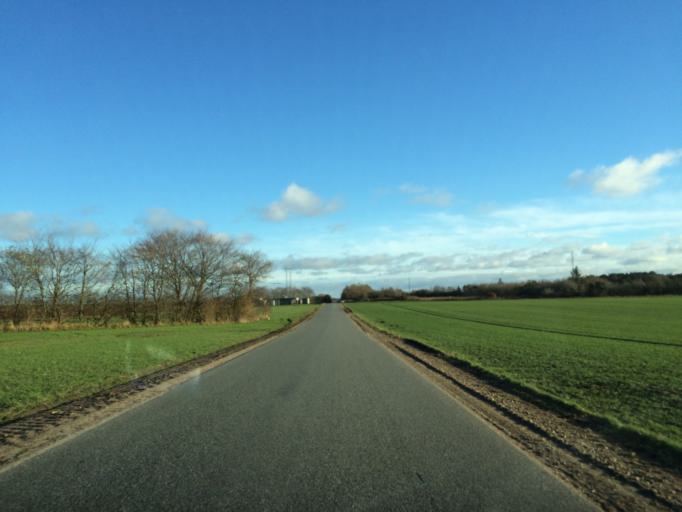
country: DK
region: Central Jutland
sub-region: Herning Kommune
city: Kibaek
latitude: 56.0411
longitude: 8.8313
